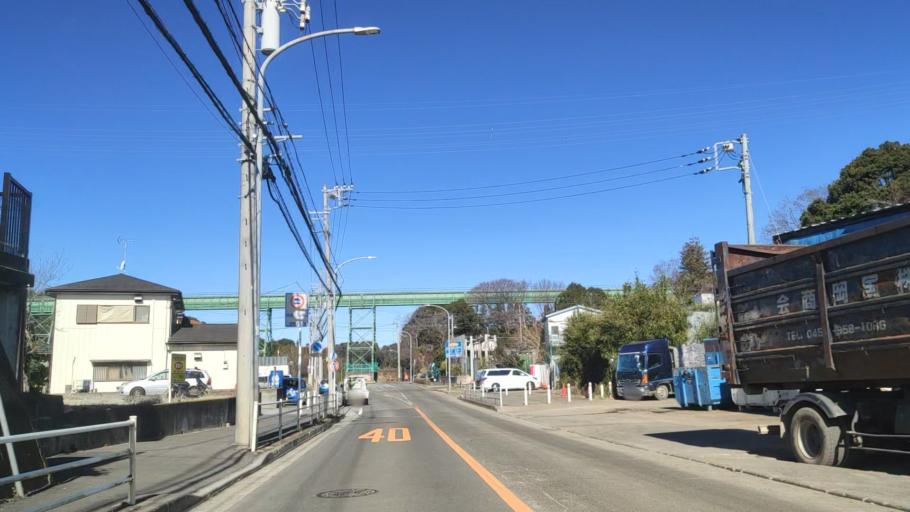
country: JP
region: Kanagawa
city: Minami-rinkan
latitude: 35.4979
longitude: 139.5151
